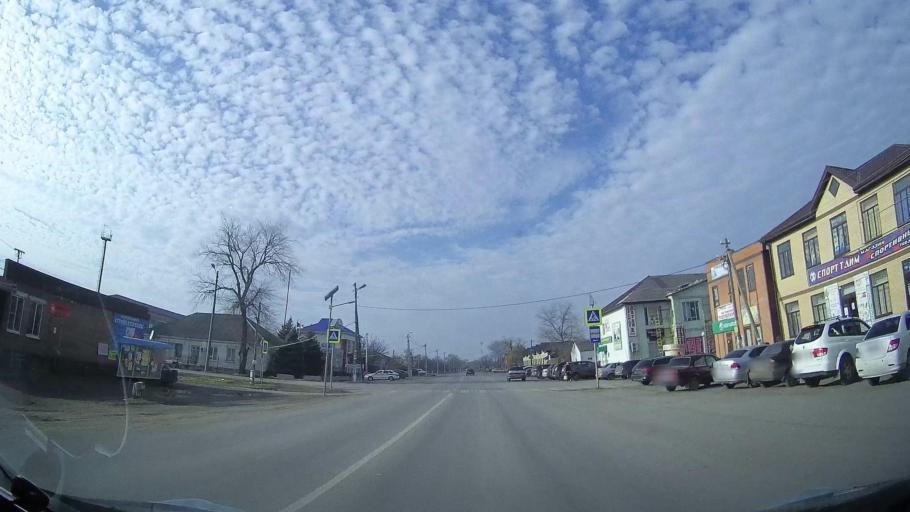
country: RU
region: Rostov
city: Veselyy
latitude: 47.0915
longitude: 40.7424
